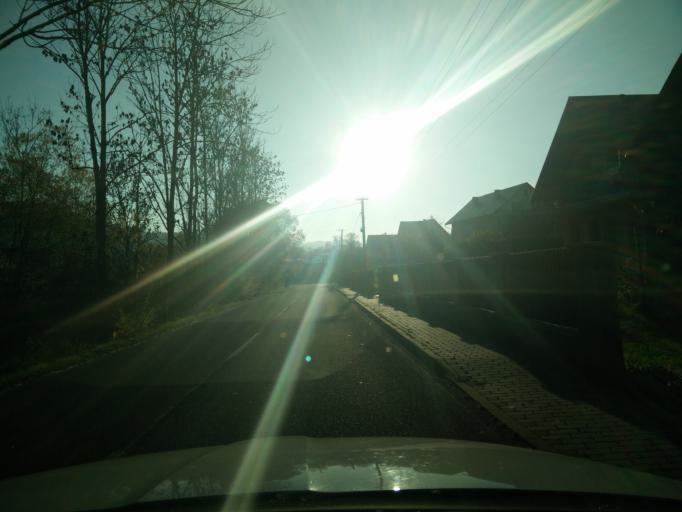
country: PL
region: Silesian Voivodeship
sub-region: Powiat zywiecki
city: Rycerka Gorna
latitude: 49.3666
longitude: 19.0525
